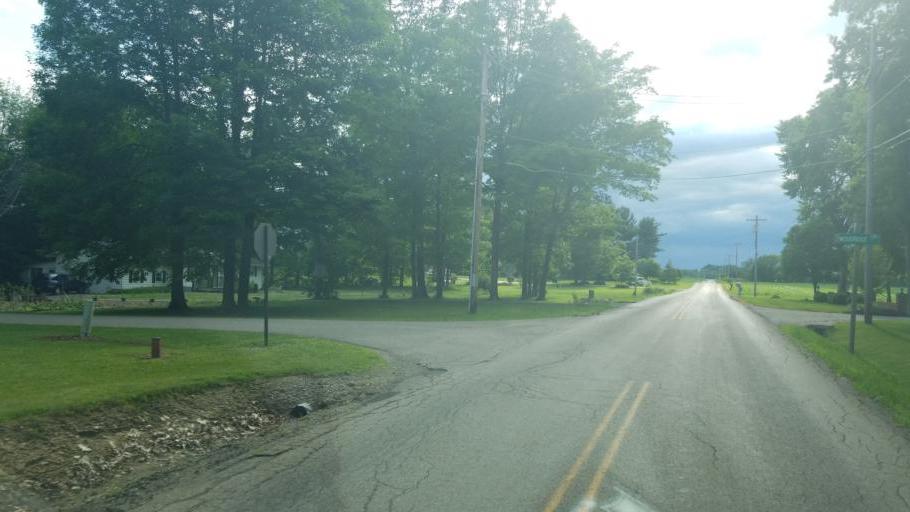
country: US
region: Ohio
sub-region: Knox County
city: Fredericktown
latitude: 40.4947
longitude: -82.5681
